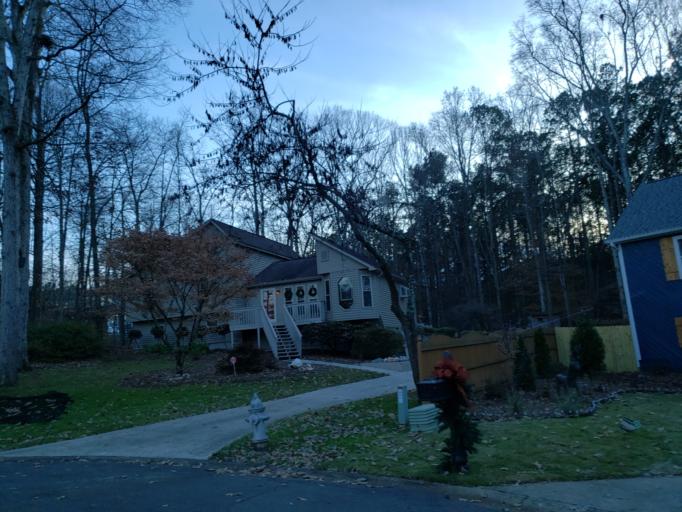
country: US
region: Georgia
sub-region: Cobb County
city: Acworth
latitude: 34.0484
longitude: -84.6505
